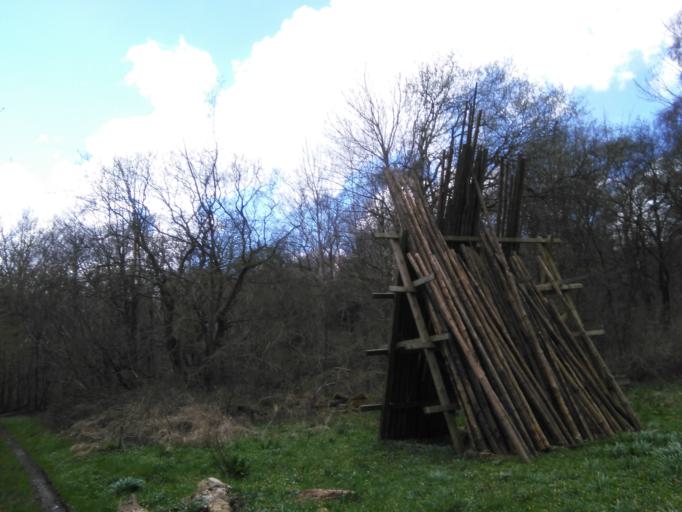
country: DK
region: Central Jutland
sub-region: Arhus Kommune
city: Trige
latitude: 56.2354
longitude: 10.1787
